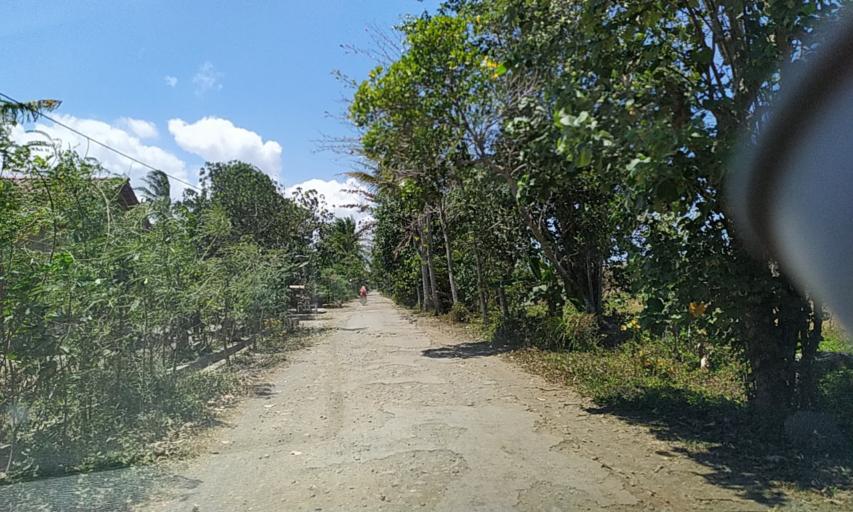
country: ID
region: Central Java
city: Mernek
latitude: -7.6228
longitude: 109.1753
